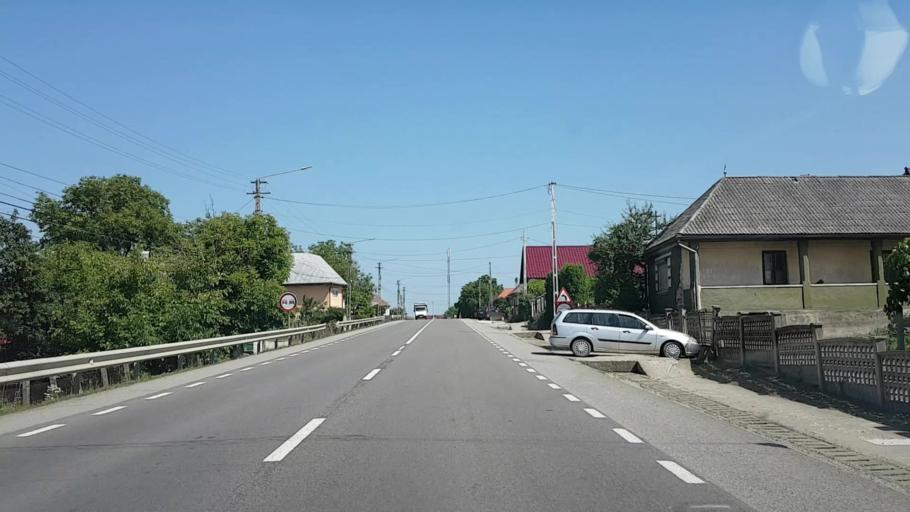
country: RO
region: Bistrita-Nasaud
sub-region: Comuna Uriu
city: Cristestii Ciceului
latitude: 47.1904
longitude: 24.1008
